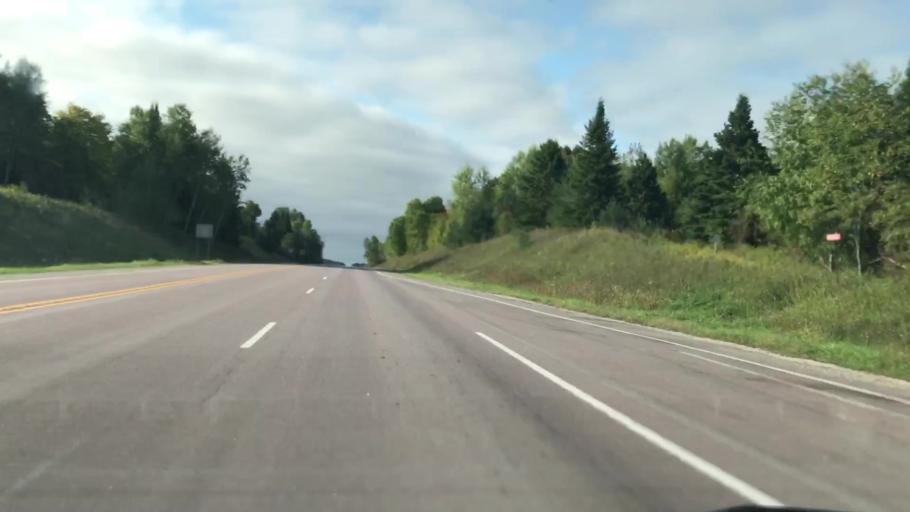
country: US
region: Michigan
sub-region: Luce County
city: Newberry
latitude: 46.3087
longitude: -85.5674
